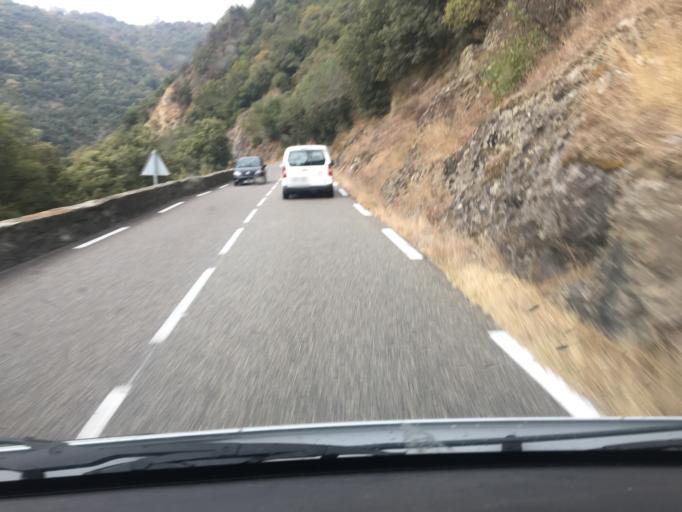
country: FR
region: Rhone-Alpes
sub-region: Departement de l'Ardeche
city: Saint-Jean-de-Muzols
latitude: 45.0627
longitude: 4.7860
